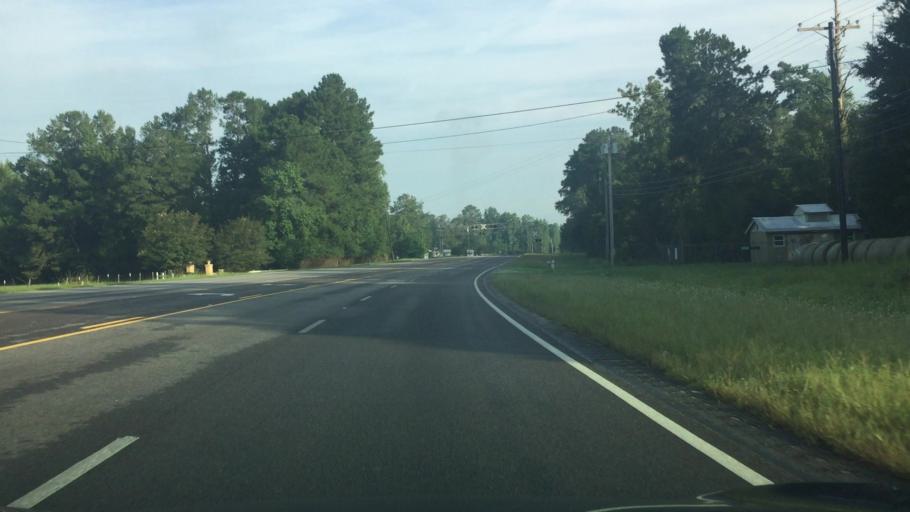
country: US
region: Alabama
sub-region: Covington County
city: Andalusia
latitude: 31.3348
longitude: -86.5192
